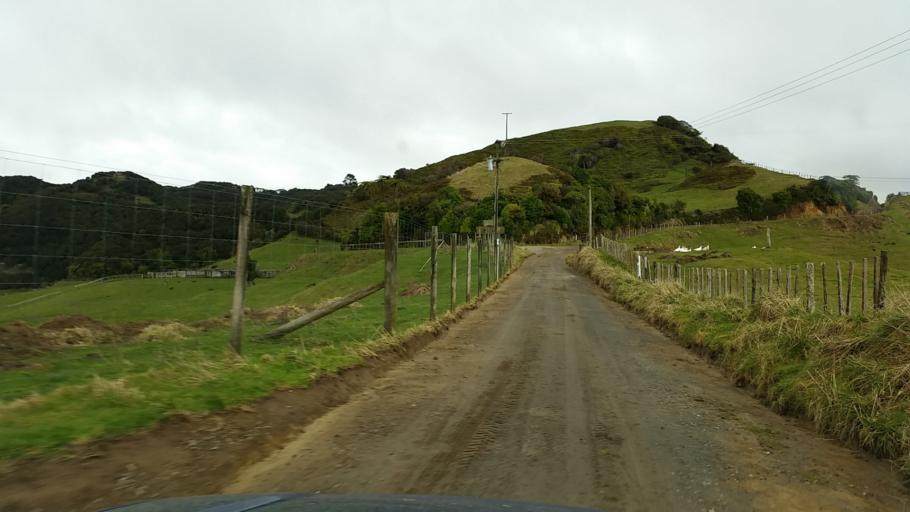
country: NZ
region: Taranaki
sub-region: South Taranaki District
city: Eltham
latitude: -39.4390
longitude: 174.6415
